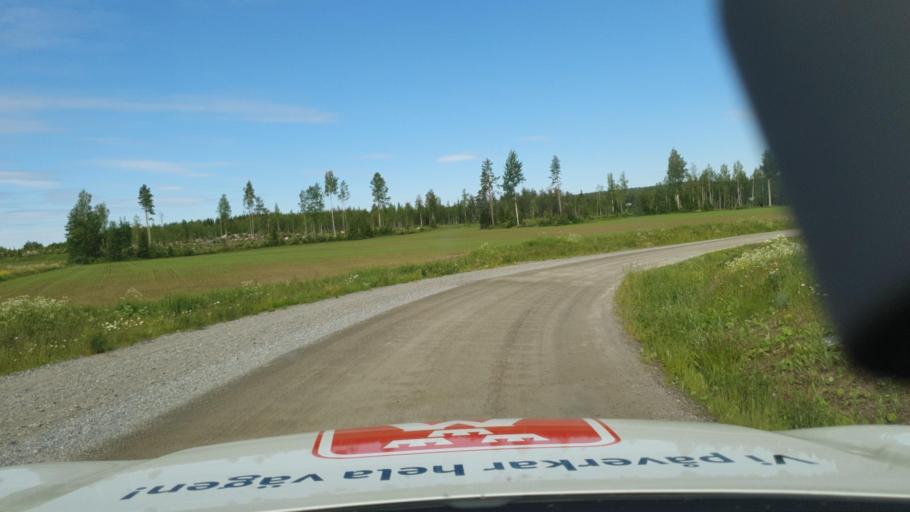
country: SE
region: Vaesterbotten
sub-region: Skelleftea Kommun
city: Forsbacka
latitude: 64.6790
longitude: 20.5195
